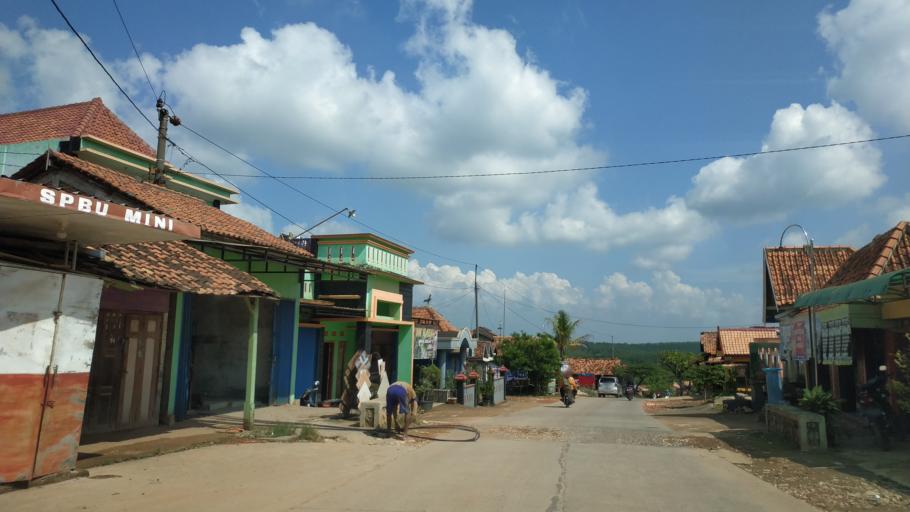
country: ID
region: Central Java
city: Jepang
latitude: -7.0107
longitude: 111.1177
